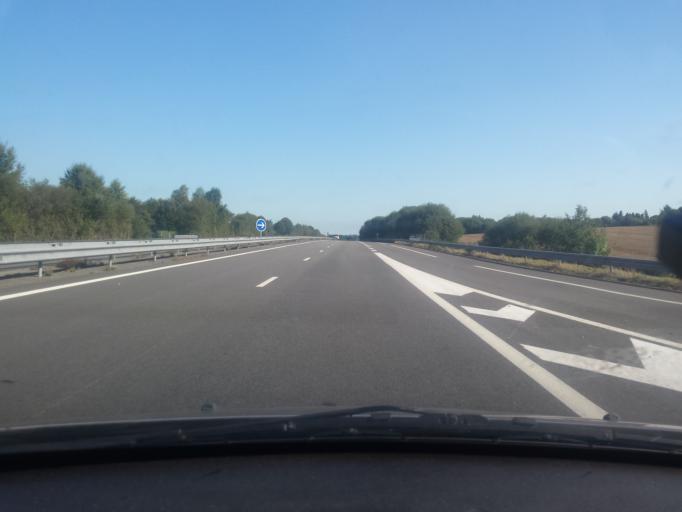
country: FR
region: Brittany
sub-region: Departement du Morbihan
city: Saint-Thuriau
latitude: 48.0007
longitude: -2.8954
